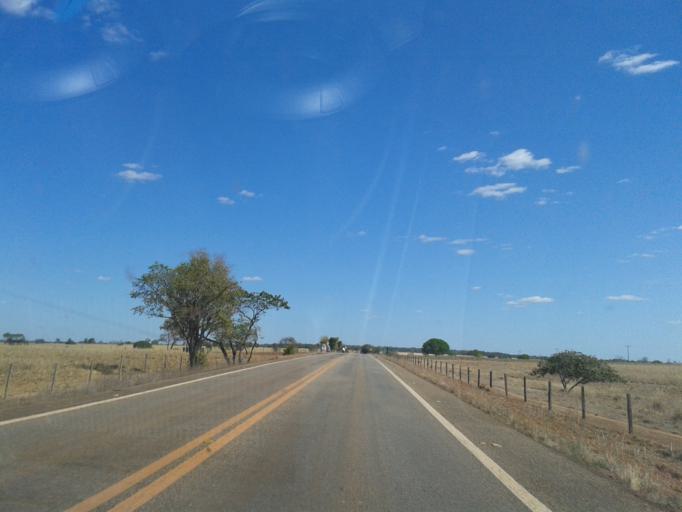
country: BR
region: Goias
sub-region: Sao Miguel Do Araguaia
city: Sao Miguel do Araguaia
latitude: -13.4414
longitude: -50.2892
